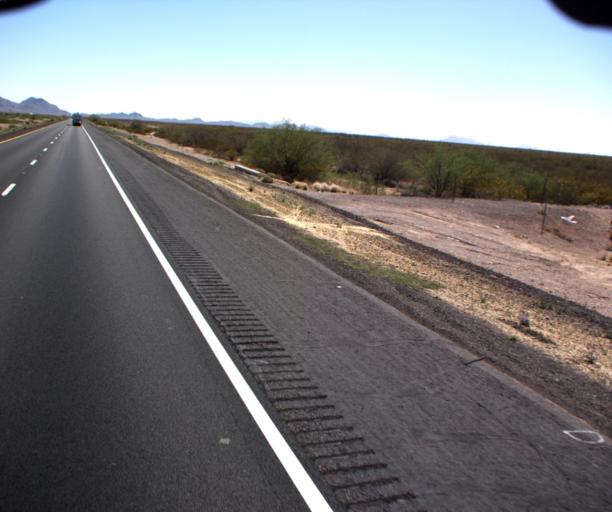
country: US
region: Arizona
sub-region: La Paz County
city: Salome
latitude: 33.6264
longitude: -113.7382
